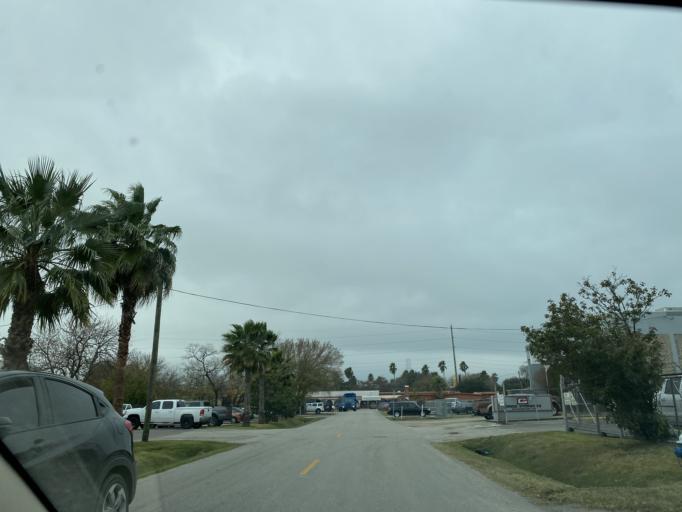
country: US
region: Texas
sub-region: Harris County
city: Bellaire
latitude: 29.7288
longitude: -95.4826
